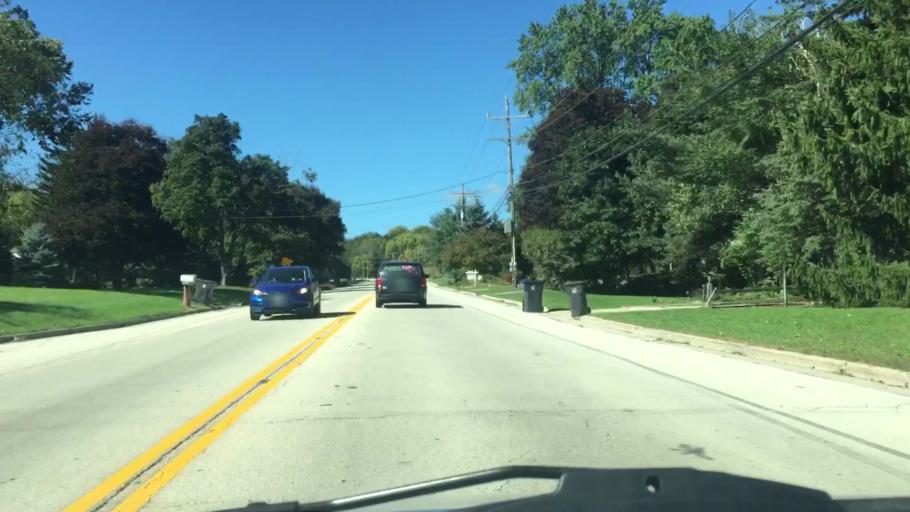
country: US
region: Wisconsin
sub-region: Waukesha County
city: Waukesha
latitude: 43.0215
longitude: -88.2910
